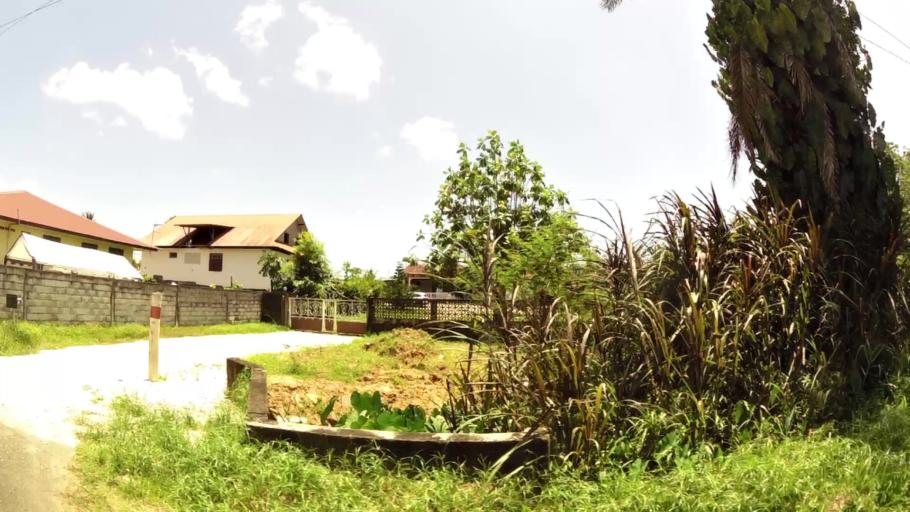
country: GF
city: Macouria
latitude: 4.8870
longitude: -52.3401
